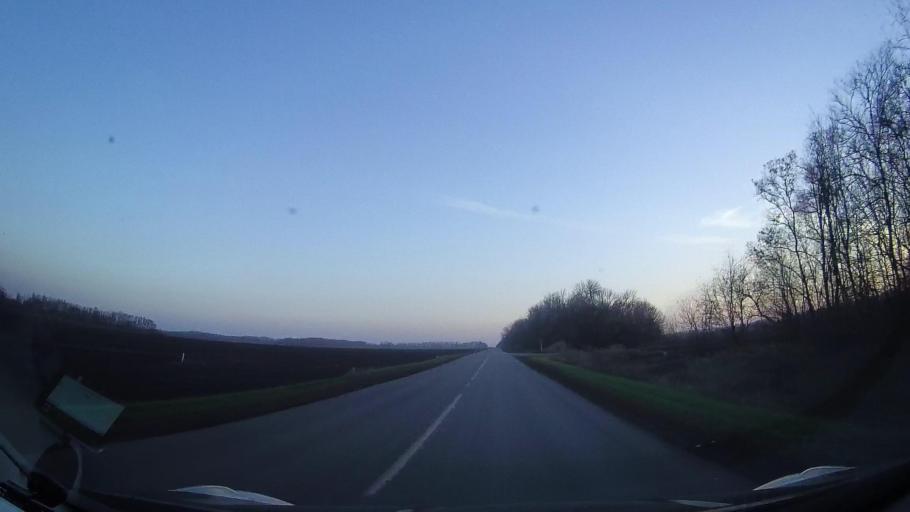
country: RU
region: Rostov
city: Zernograd
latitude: 47.0022
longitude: 40.3915
